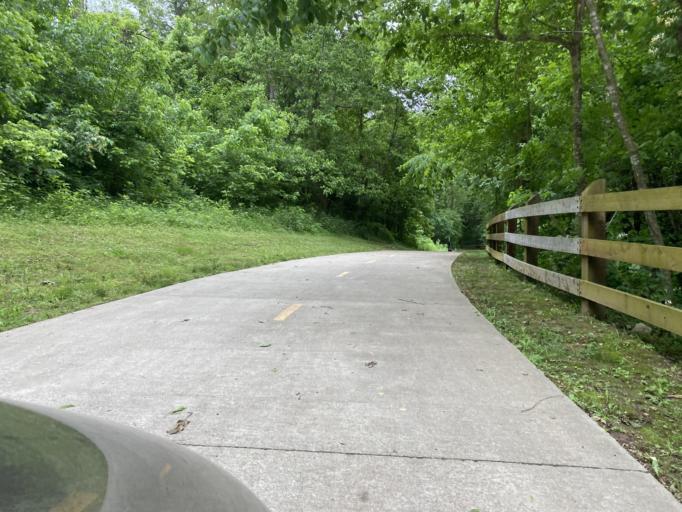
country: US
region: Arkansas
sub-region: Benton County
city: Bentonville
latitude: 36.3746
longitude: -94.2378
